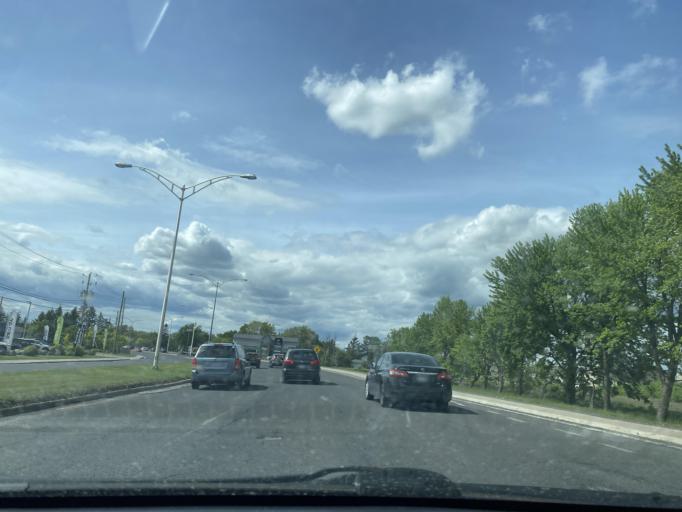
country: CA
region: Quebec
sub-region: Monteregie
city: Carignan
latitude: 45.4574
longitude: -73.3029
